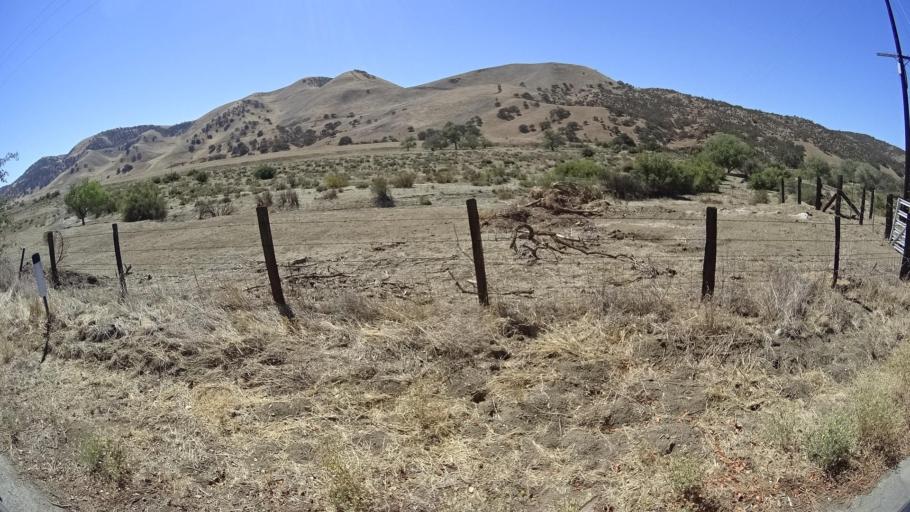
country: US
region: California
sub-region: Monterey County
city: King City
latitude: 36.2826
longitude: -120.9590
